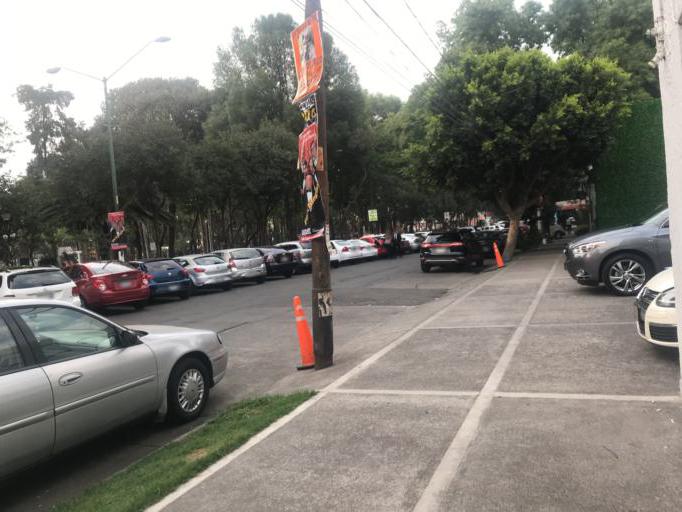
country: MX
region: Mexico City
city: Colonia del Valle
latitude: 19.3777
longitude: -99.1616
